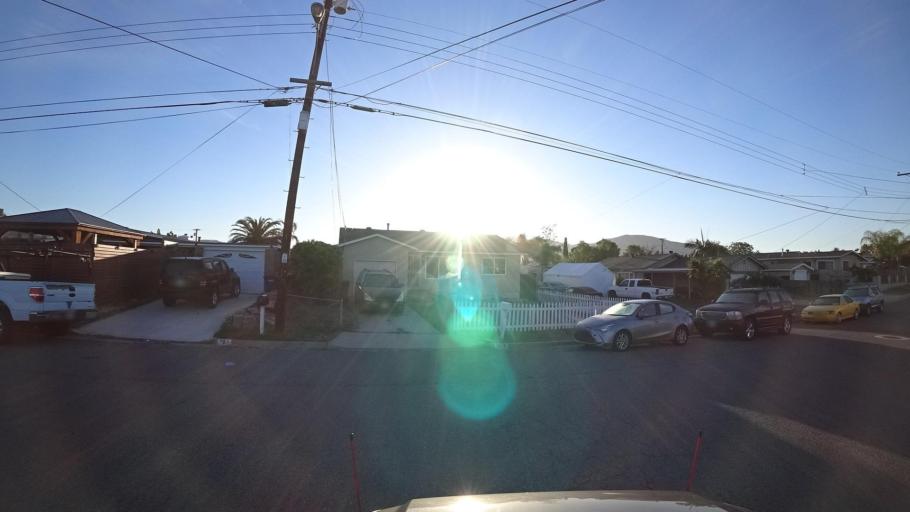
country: US
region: California
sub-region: San Diego County
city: La Presa
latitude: 32.7097
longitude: -116.9917
